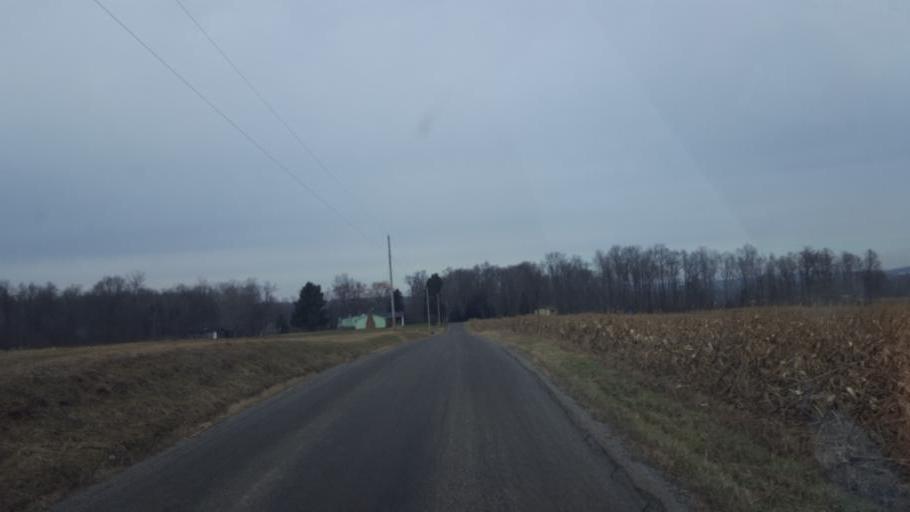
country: US
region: Ohio
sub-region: Richland County
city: Lexington
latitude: 40.6129
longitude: -82.6153
